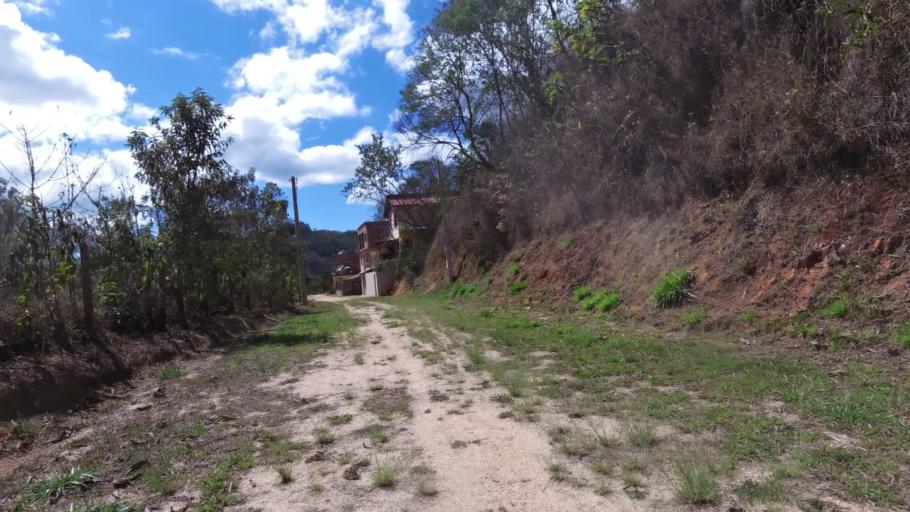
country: BR
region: Espirito Santo
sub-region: Vargem Alta
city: Vargem Alta
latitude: -20.6749
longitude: -41.0095
